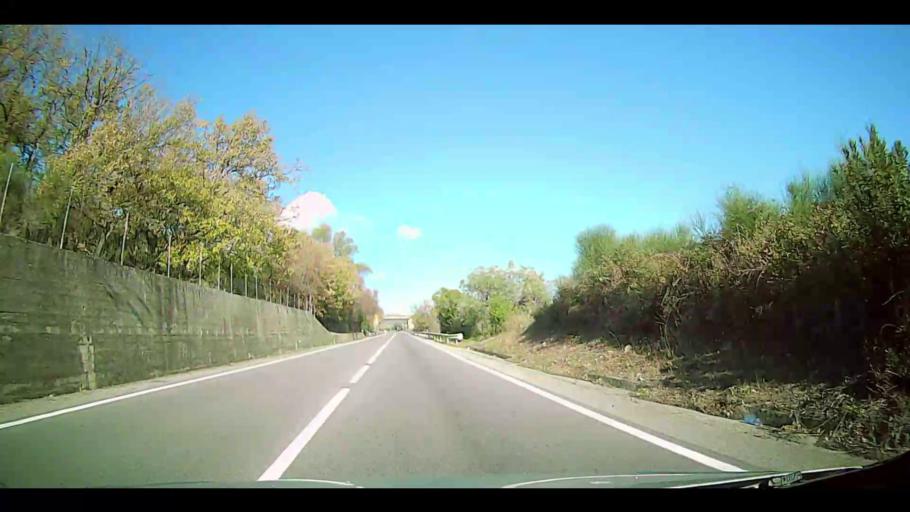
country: IT
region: Calabria
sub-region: Provincia di Crotone
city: Caccuri
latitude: 39.2050
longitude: 16.8060
